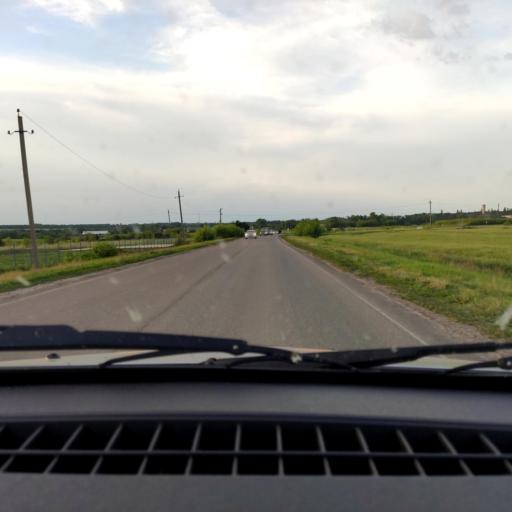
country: RU
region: Voronezj
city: Ramon'
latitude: 51.9336
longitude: 39.3320
